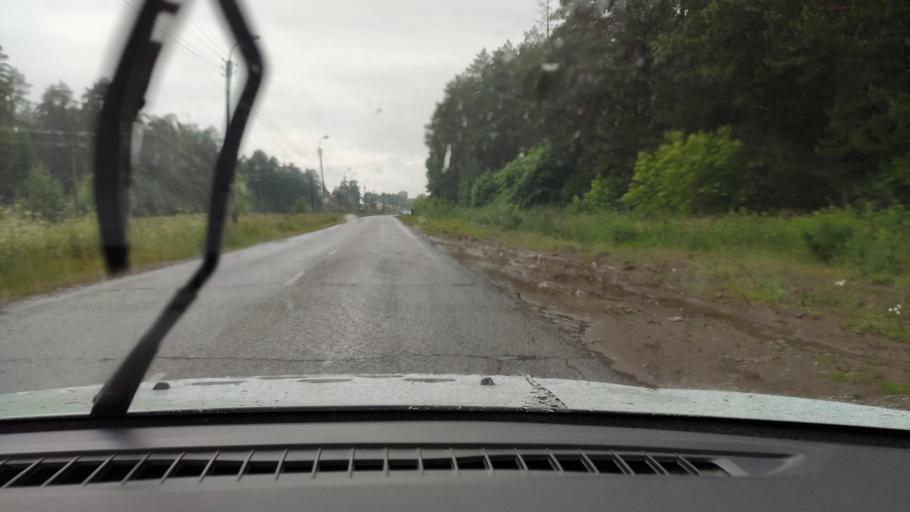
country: RU
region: Udmurtiya
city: Votkinsk
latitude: 57.0668
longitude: 54.0328
